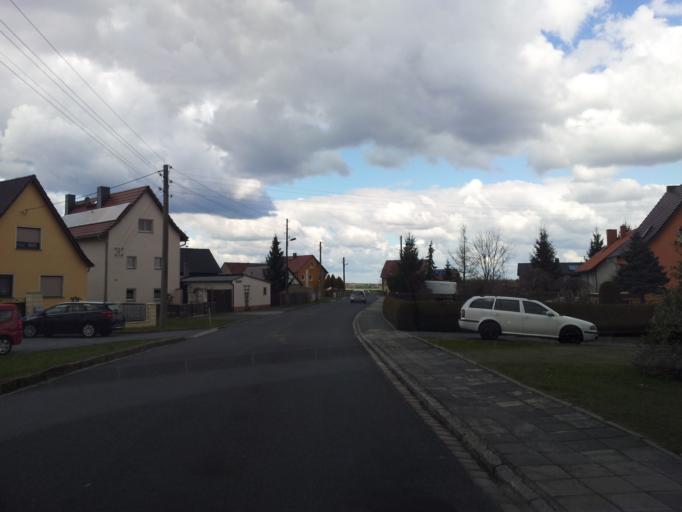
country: DE
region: Saxony
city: Horka
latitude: 51.2898
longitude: 14.2270
